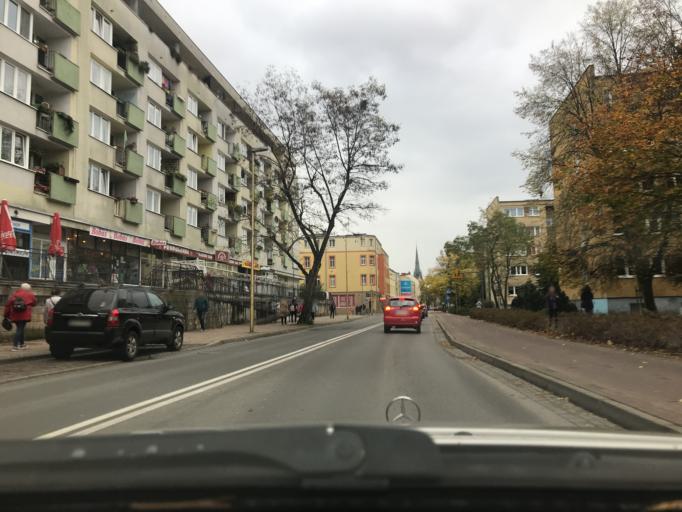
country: PL
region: West Pomeranian Voivodeship
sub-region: Swinoujscie
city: Swinoujscie
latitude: 53.9115
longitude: 14.2420
